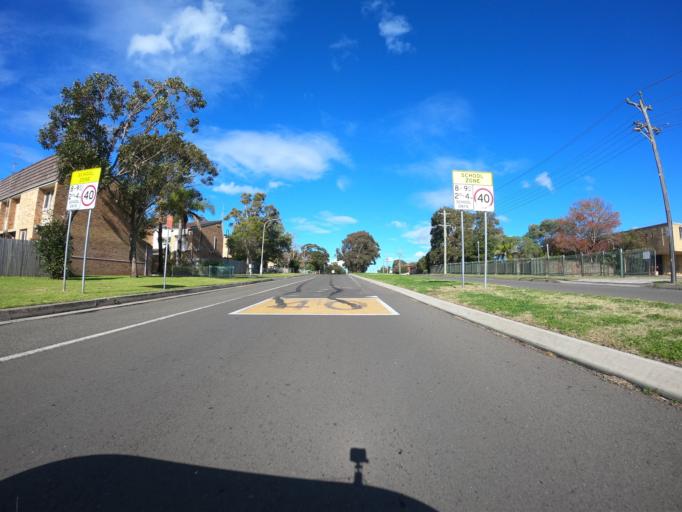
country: AU
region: New South Wales
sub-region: Wollongong
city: East Corrimal
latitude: -34.3654
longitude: 150.9172
